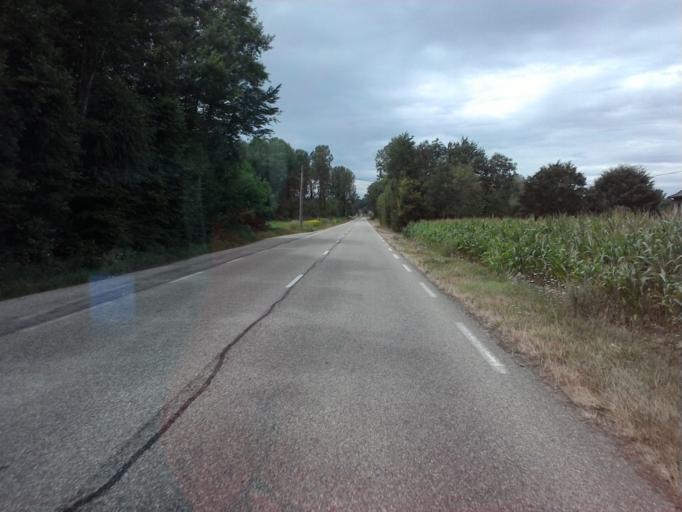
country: FR
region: Rhone-Alpes
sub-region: Departement de l'Isere
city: La Batie-Montgascon
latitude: 45.5817
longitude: 5.5617
